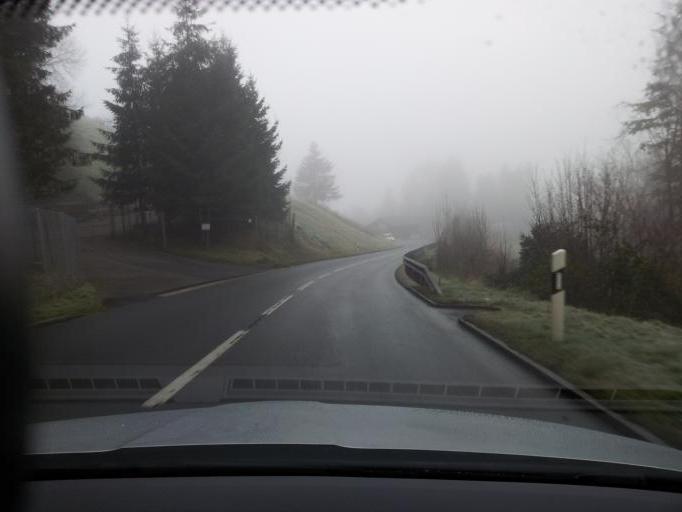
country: CH
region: Lucerne
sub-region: Lucerne-Stadt District
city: Littau
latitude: 47.0410
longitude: 8.2398
